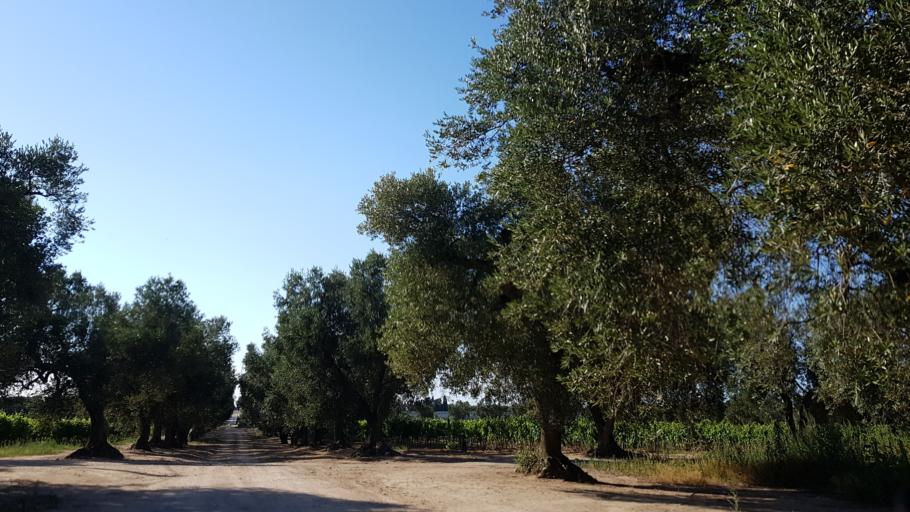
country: IT
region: Apulia
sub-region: Provincia di Brindisi
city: La Rosa
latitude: 40.5897
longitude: 17.9888
